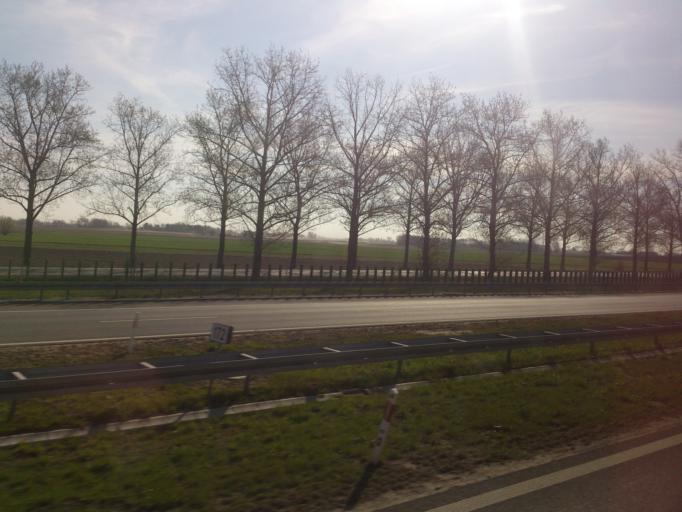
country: PL
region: Kujawsko-Pomorskie
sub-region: Powiat aleksandrowski
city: Raciazek
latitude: 52.8123
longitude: 18.8120
